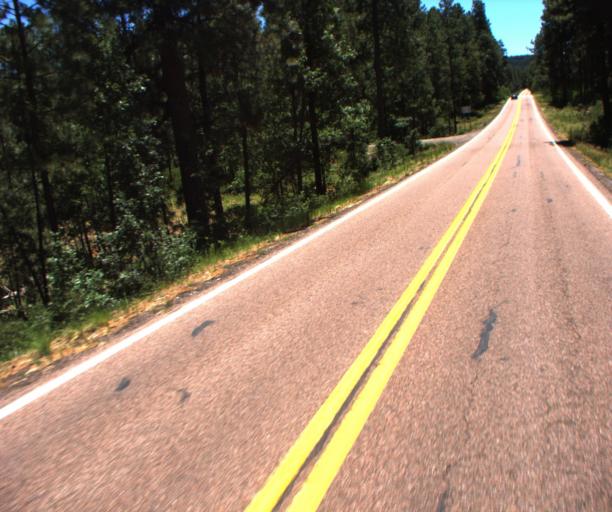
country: US
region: Arizona
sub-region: Gila County
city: Pine
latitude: 34.4792
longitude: -111.3814
